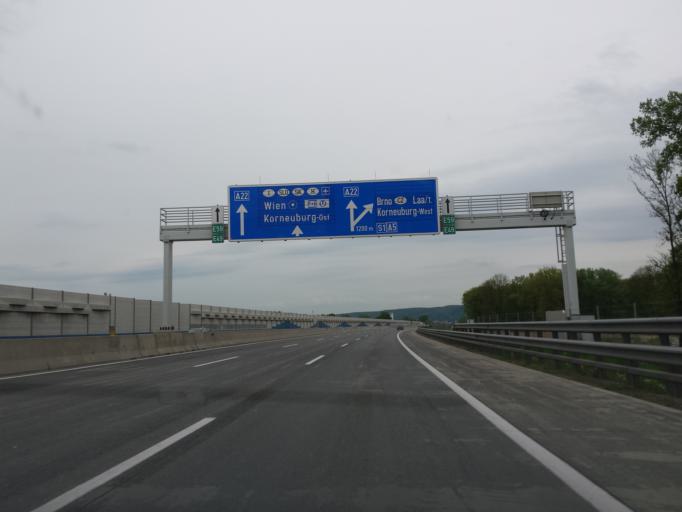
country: AT
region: Lower Austria
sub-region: Politischer Bezirk Korneuburg
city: Leobendorf
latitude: 48.3678
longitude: 16.2961
